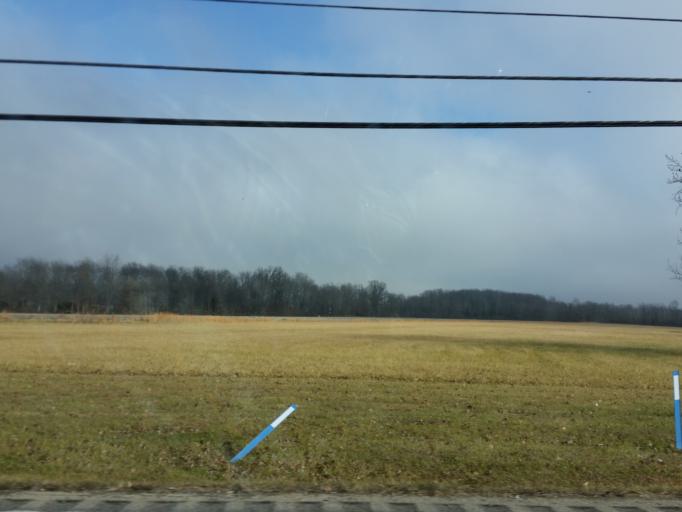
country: US
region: Indiana
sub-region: Jefferson County
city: North Madison
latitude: 38.7786
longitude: -85.4220
